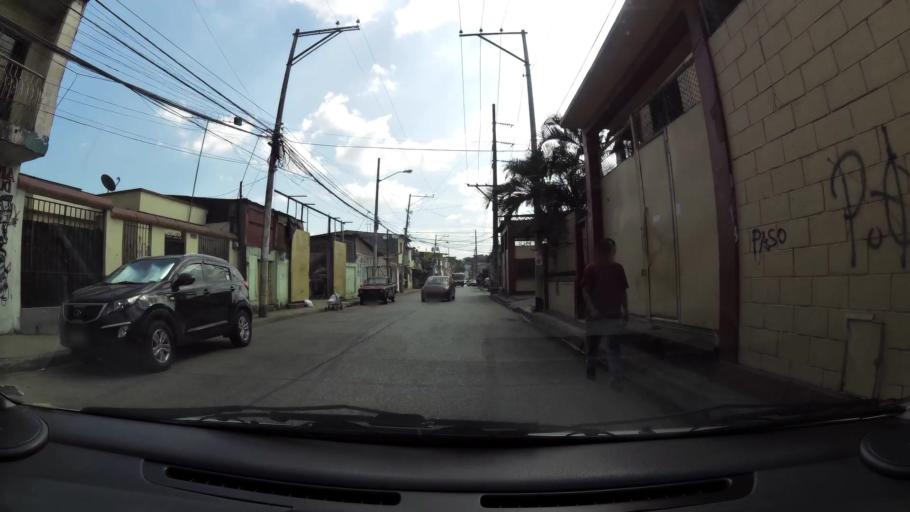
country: EC
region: Guayas
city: Guayaquil
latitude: -2.1414
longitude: -79.9372
